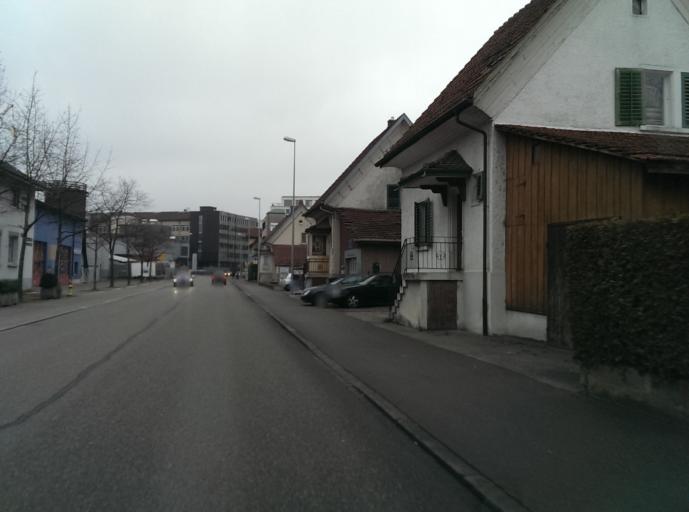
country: CH
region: Zurich
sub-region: Bezirk Dietikon
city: Dietikon / Vorstadt
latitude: 47.4124
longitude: 8.4025
